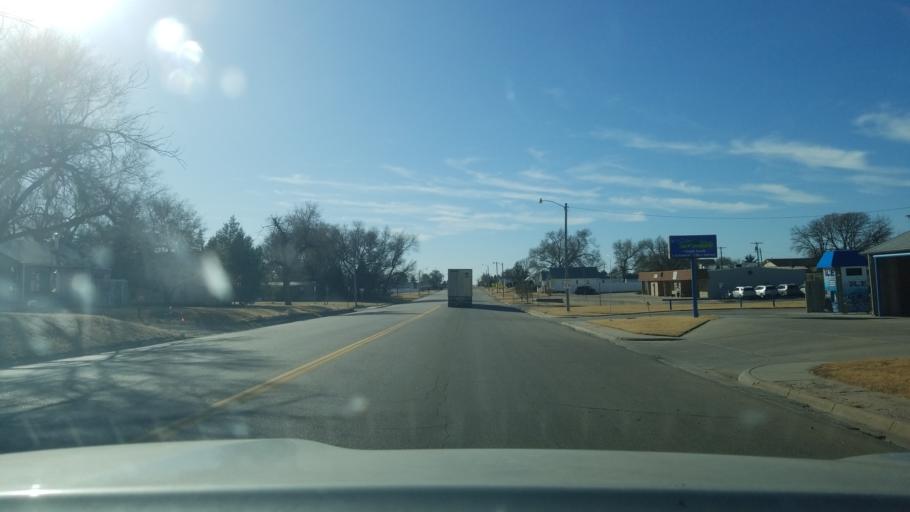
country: US
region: Kansas
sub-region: Ness County
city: Ness City
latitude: 38.4503
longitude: -99.9050
